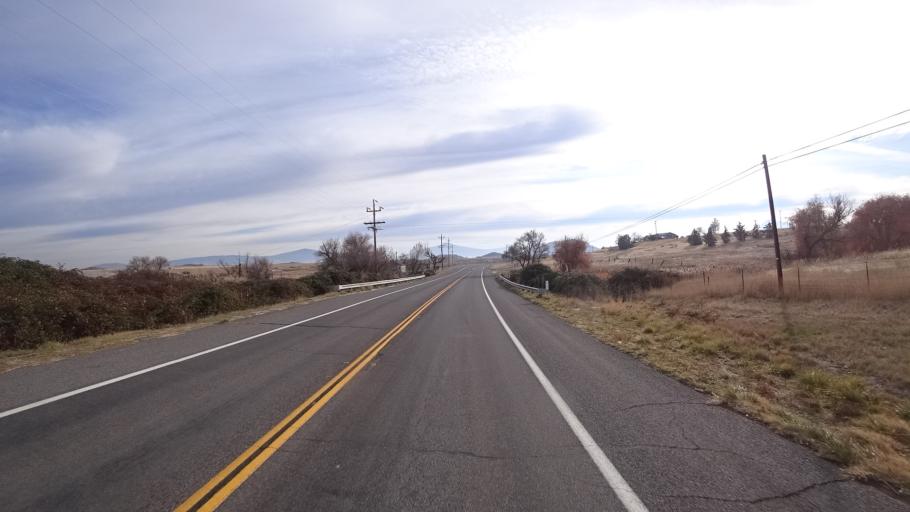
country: US
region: California
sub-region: Siskiyou County
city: Montague
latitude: 41.7291
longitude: -122.5660
